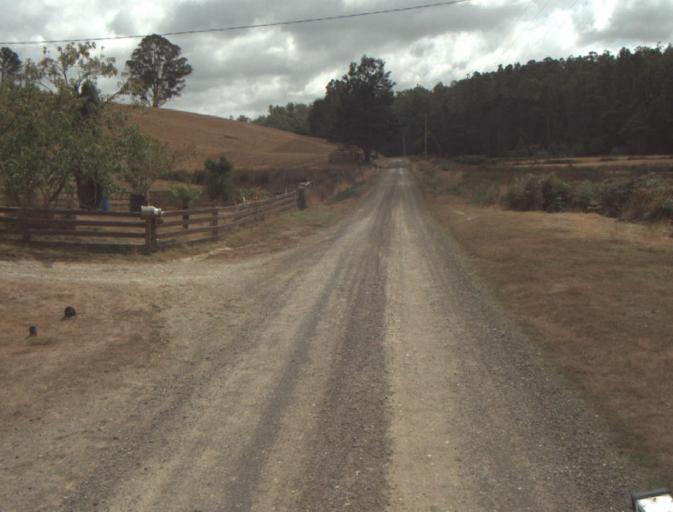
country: AU
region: Tasmania
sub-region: Dorset
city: Bridport
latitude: -41.1883
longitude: 147.2617
